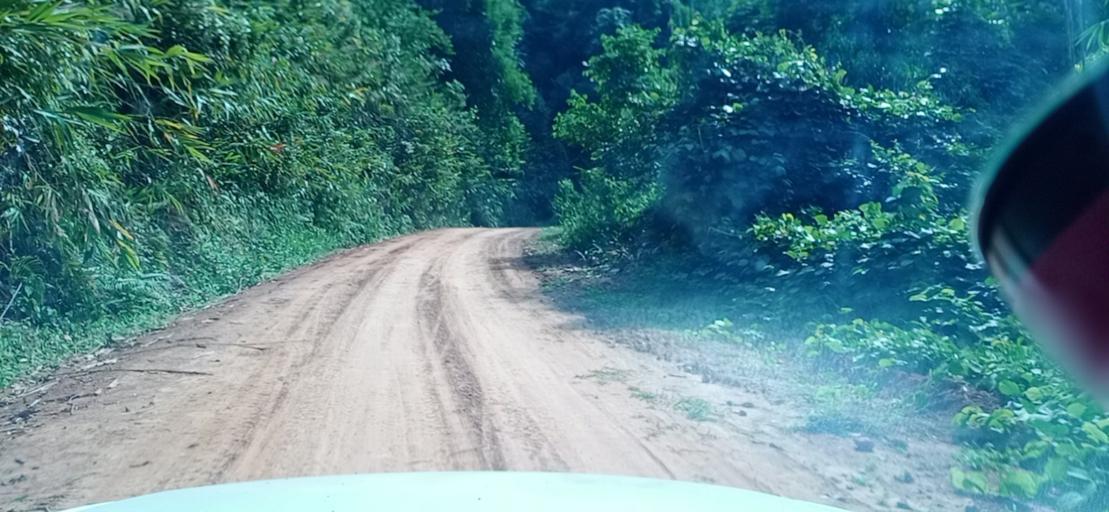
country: TH
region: Changwat Bueng Kan
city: Pak Khat
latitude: 18.6362
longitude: 103.2594
